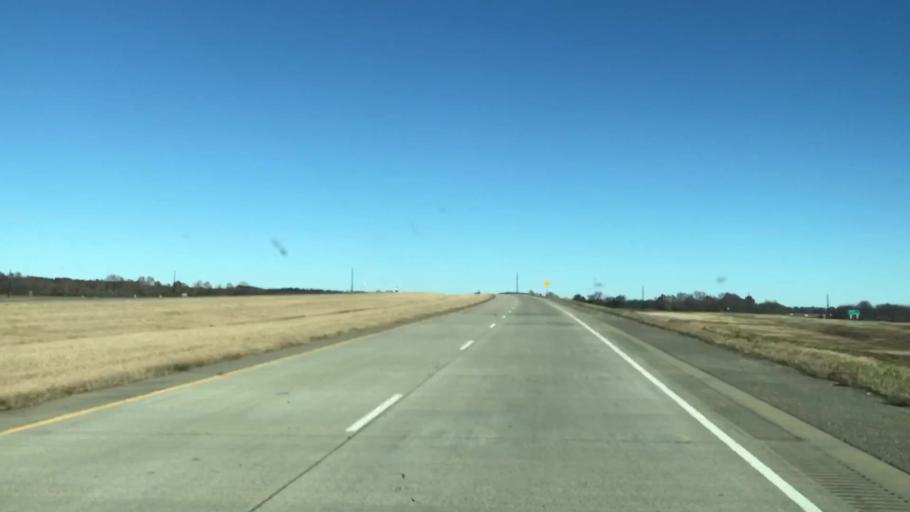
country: US
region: Louisiana
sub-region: Caddo Parish
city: Vivian
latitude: 32.8934
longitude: -93.8602
